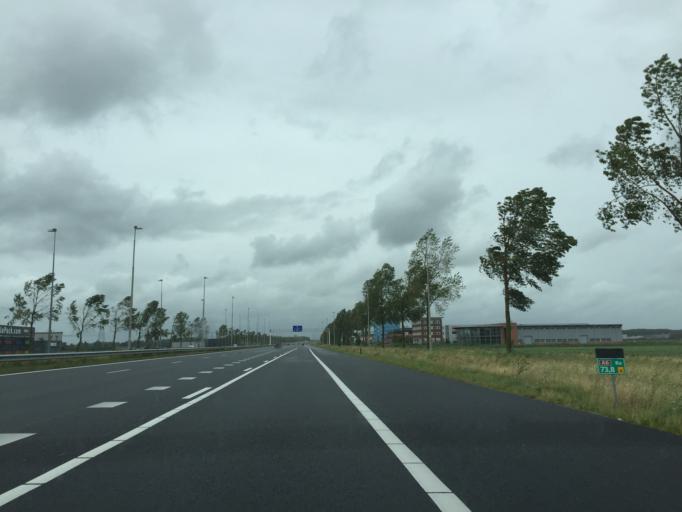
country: NL
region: Flevoland
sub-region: Gemeente Lelystad
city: Lelystad
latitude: 52.4712
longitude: 5.4843
